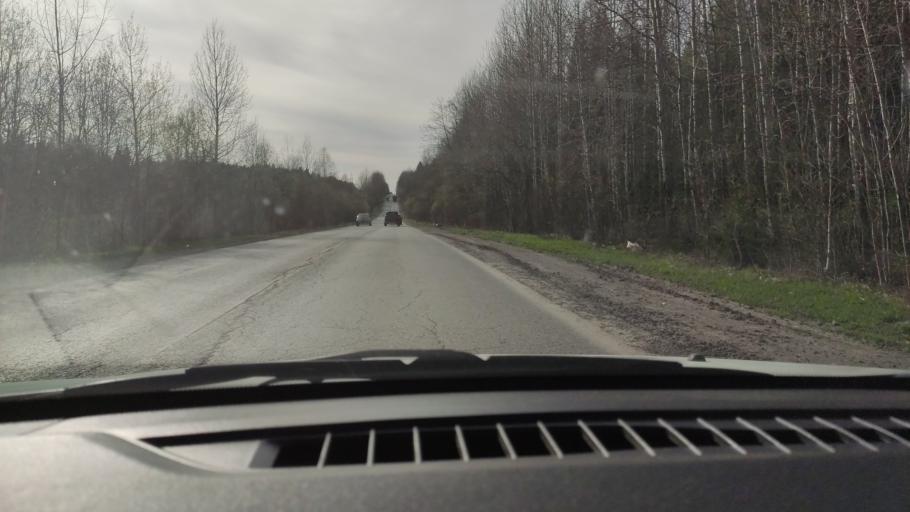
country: RU
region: Perm
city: Ferma
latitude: 57.9360
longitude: 56.4688
